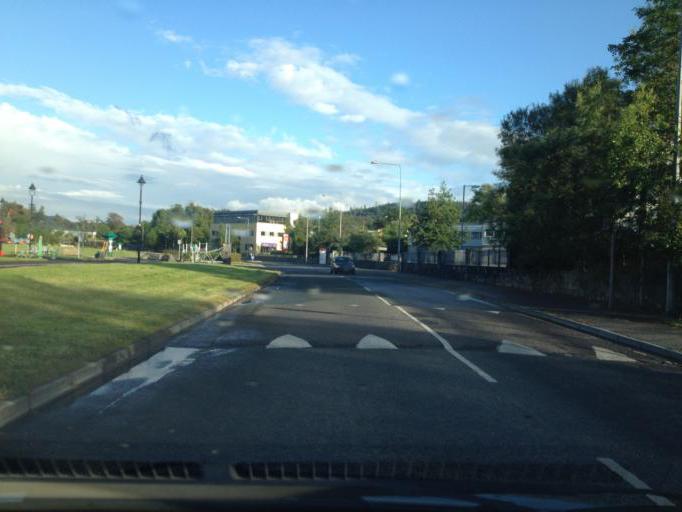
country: IE
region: Connaught
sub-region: Sligo
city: Sligo
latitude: 54.2674
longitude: -8.4552
